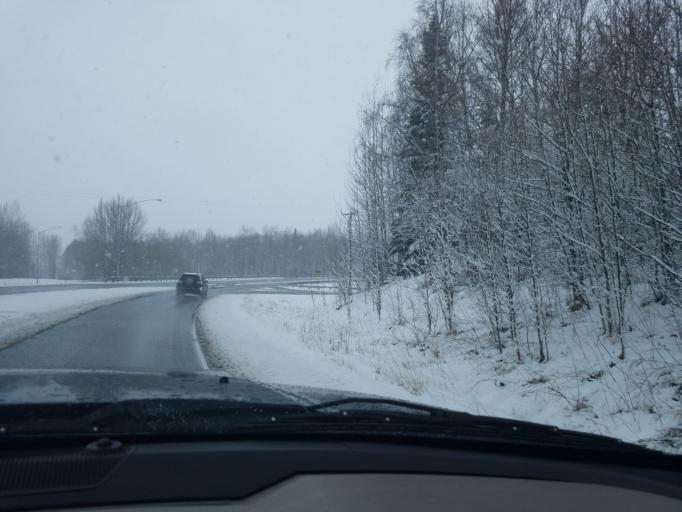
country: US
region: Alaska
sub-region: Anchorage Municipality
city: Anchorage
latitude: 61.1649
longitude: -149.9521
